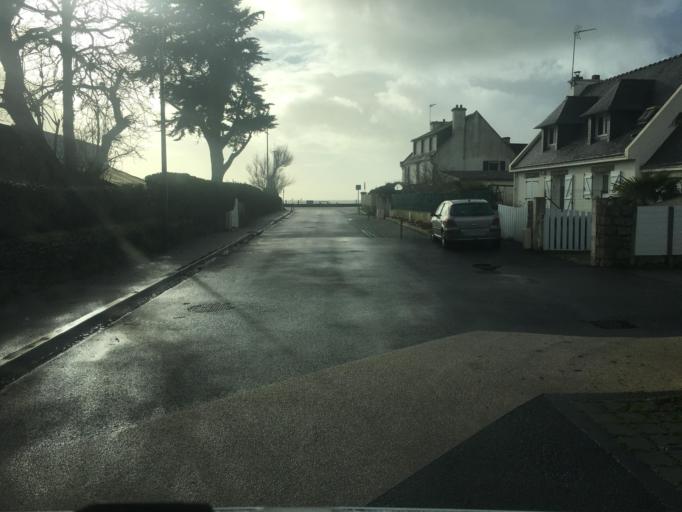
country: FR
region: Brittany
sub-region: Departement du Morbihan
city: Sarzeau
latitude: 47.4982
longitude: -2.7710
